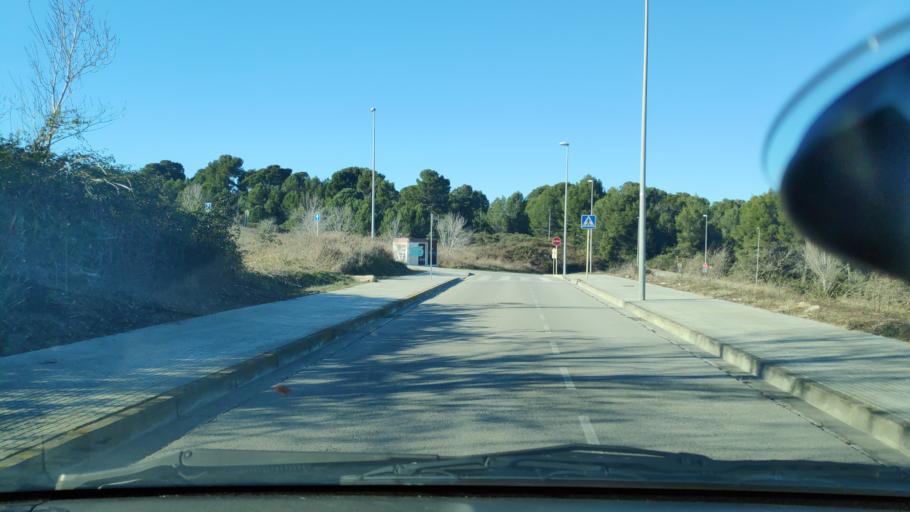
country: ES
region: Catalonia
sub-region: Provincia de Barcelona
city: Sant Quirze del Valles
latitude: 41.5371
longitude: 2.0582
